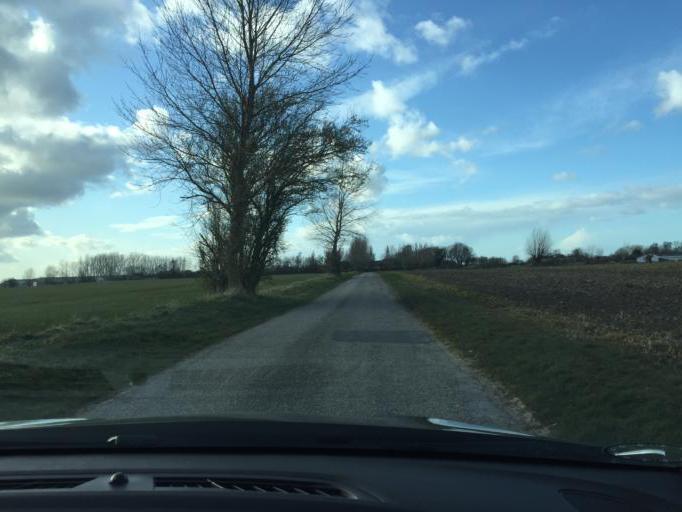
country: DK
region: South Denmark
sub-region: Nyborg Kommune
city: Ullerslev
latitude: 55.3462
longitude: 10.7224
